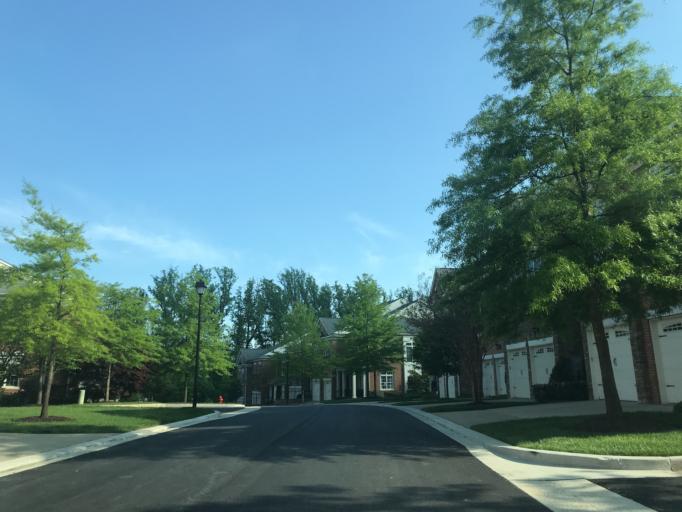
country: US
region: Maryland
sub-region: Baltimore County
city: Towson
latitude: 39.3839
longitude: -76.6217
